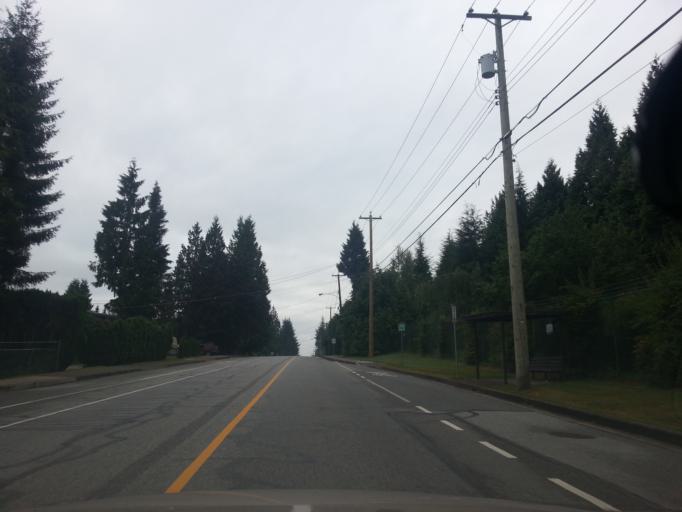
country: CA
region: British Columbia
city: Port Moody
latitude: 49.2782
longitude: -122.8809
